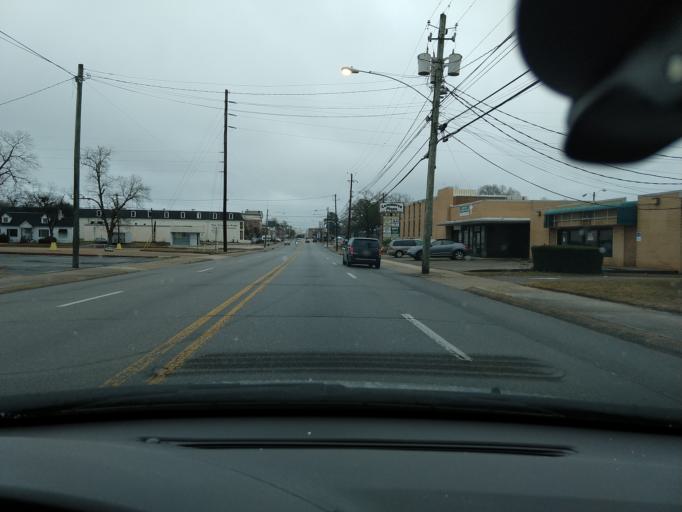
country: US
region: Alabama
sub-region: Houston County
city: Dothan
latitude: 31.2251
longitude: -85.3996
